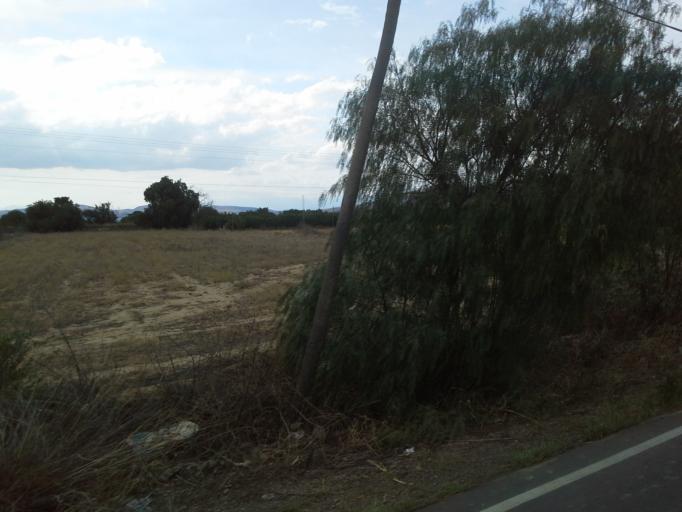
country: BO
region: Cochabamba
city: Tarata
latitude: -17.5771
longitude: -66.0149
